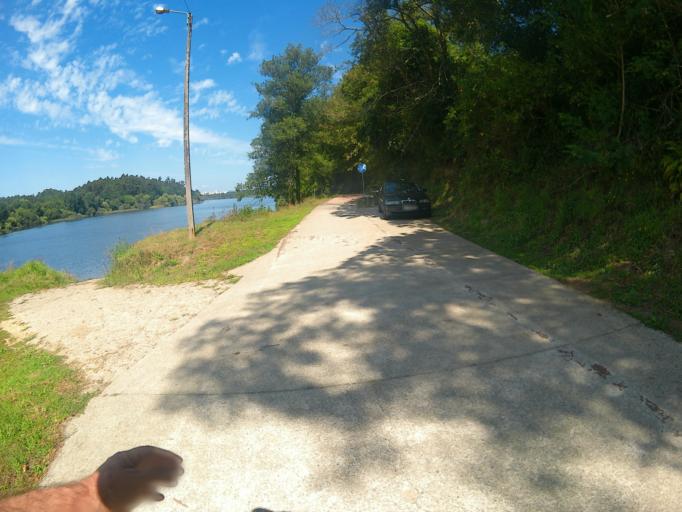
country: PT
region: Viana do Castelo
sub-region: Valenca
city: Valenca
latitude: 41.9978
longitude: -8.6694
